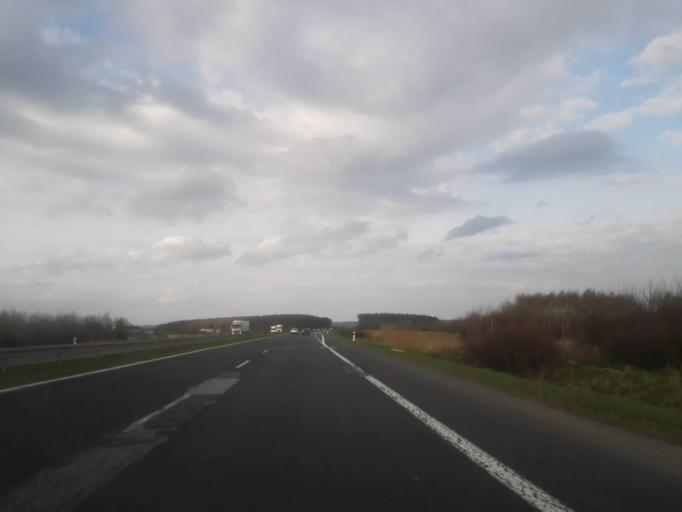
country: PL
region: Lodz Voivodeship
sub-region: Powiat piotrkowski
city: Wola Krzysztoporska
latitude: 51.2949
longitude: 19.5465
